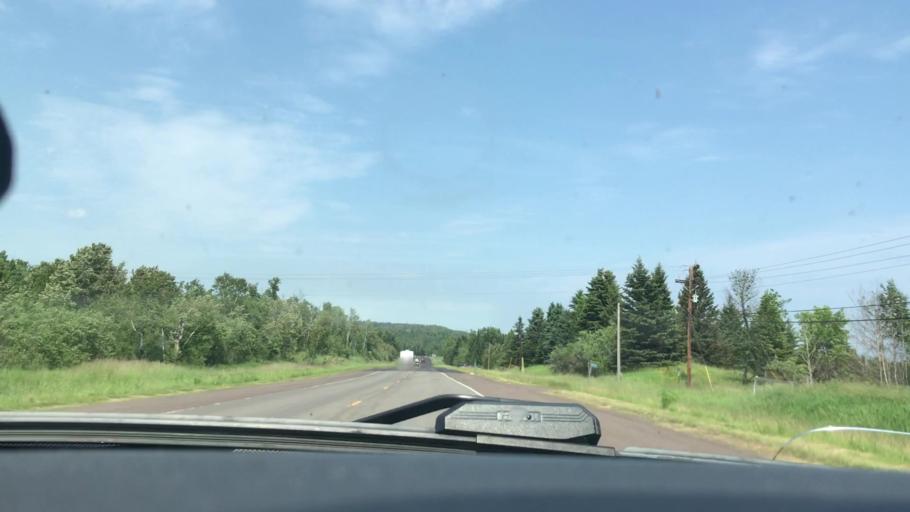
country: US
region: Minnesota
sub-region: Lake County
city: Silver Bay
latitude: 47.3275
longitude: -91.2108
